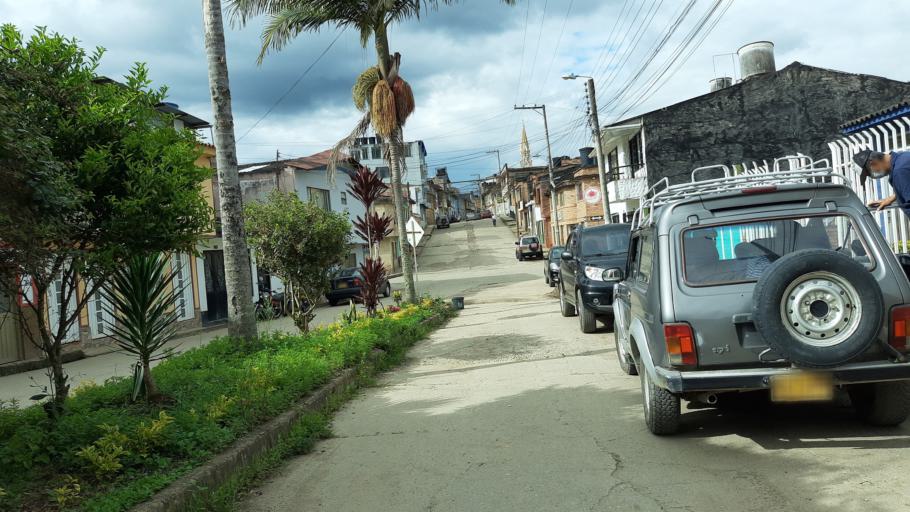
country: CO
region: Boyaca
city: Garagoa
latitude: 5.0786
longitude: -73.3640
